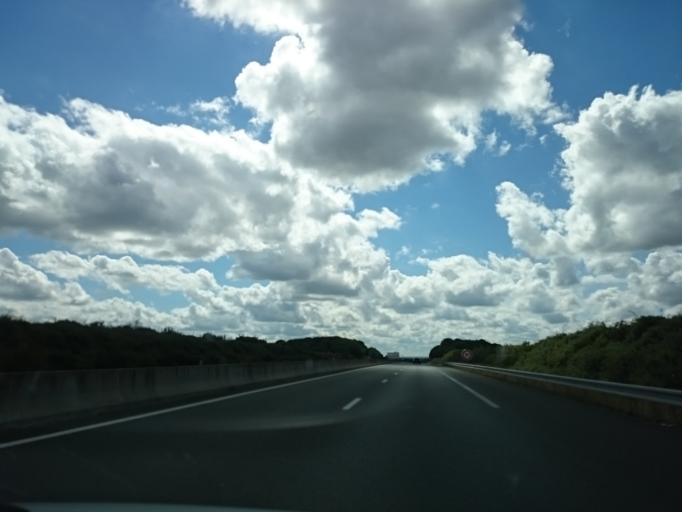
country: FR
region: Pays de la Loire
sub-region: Departement de Maine-et-Loire
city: Saint-Leger-des-Bois
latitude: 47.4650
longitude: -0.6915
